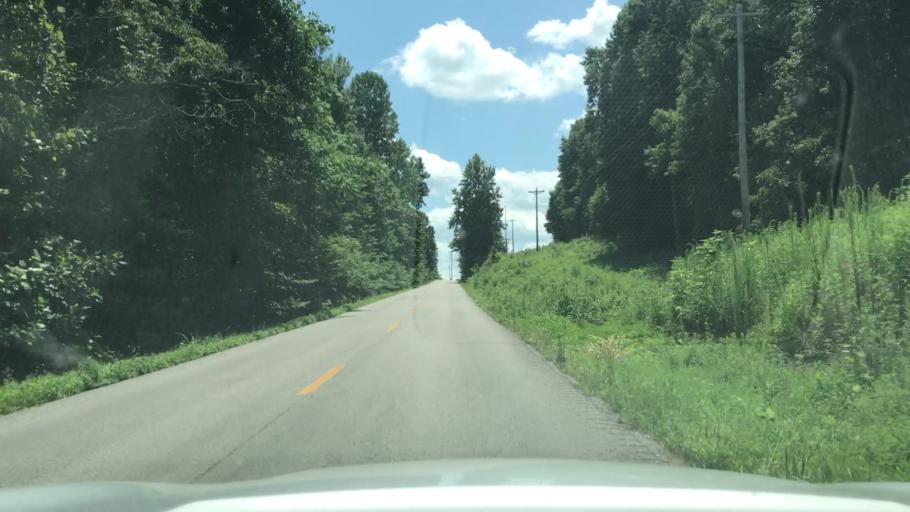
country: US
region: Kentucky
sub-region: Hopkins County
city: Nortonville
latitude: 37.0402
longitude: -87.3498
